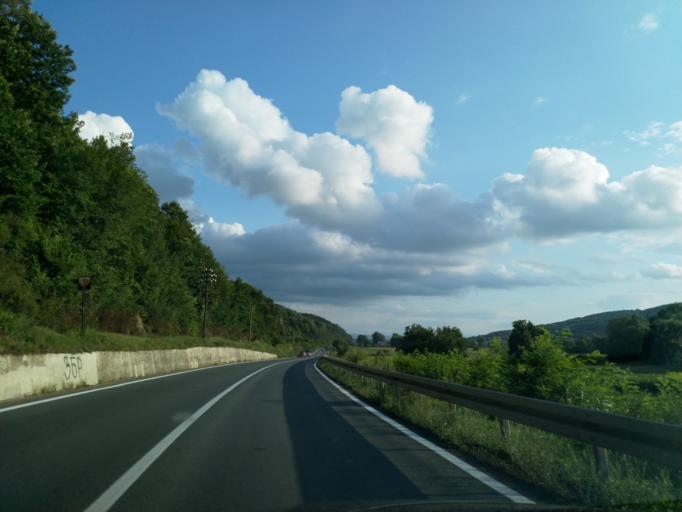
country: RS
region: Central Serbia
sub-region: Rasinski Okrug
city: Varvarin
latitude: 43.6462
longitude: 21.3834
